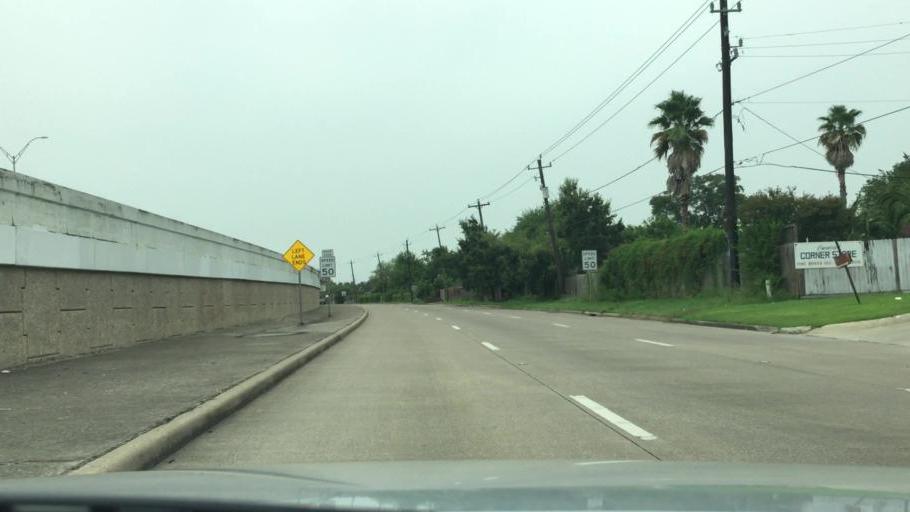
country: US
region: Texas
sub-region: Harris County
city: Cloverleaf
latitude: 29.7828
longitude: -95.1583
